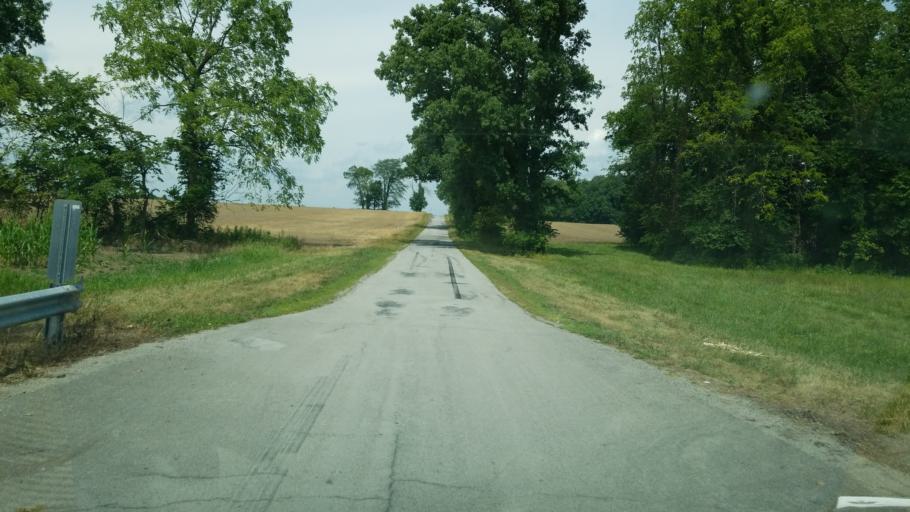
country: US
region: Ohio
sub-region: Hancock County
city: Findlay
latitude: 40.9869
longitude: -83.7466
